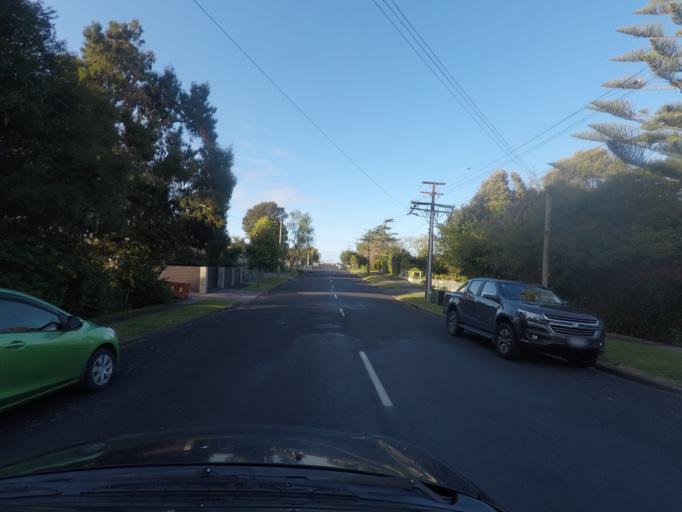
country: NZ
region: Auckland
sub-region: Auckland
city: Waitakere
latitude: -36.9075
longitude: 174.6733
